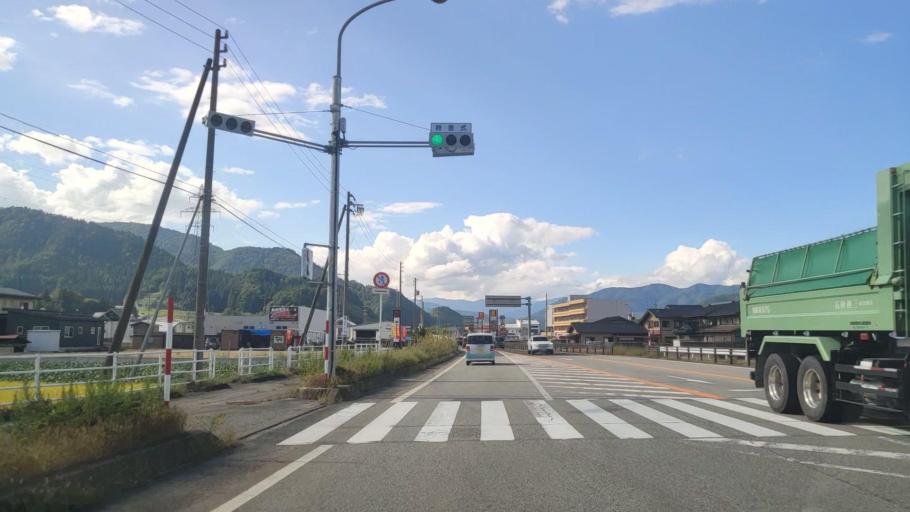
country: JP
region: Gifu
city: Takayama
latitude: 36.2261
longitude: 137.1880
